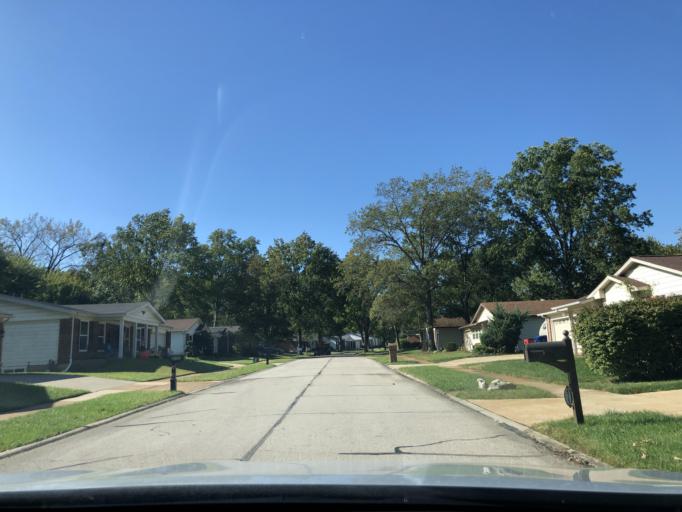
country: US
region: Missouri
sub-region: Saint Louis County
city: Concord
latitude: 38.4938
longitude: -90.3580
